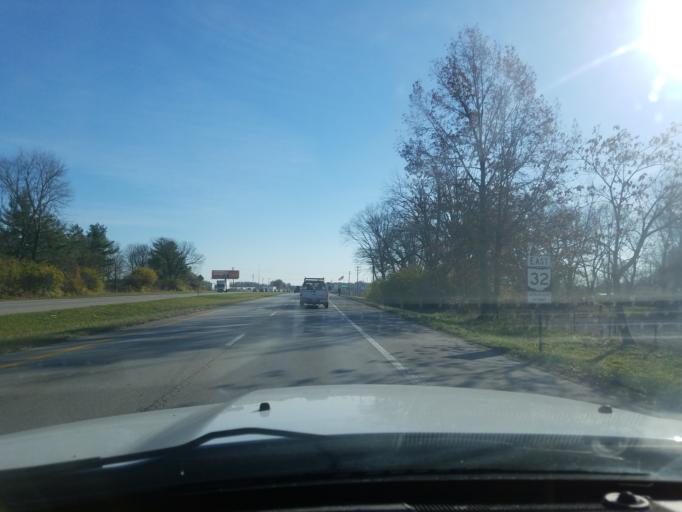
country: US
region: Ohio
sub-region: Clermont County
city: Summerside
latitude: 39.0933
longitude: -84.2578
